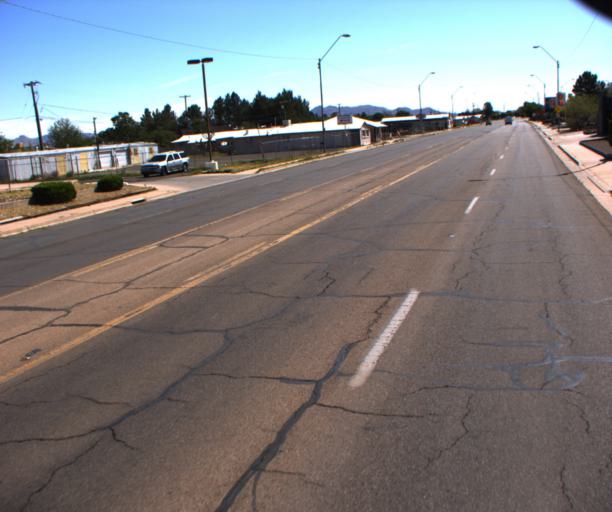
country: US
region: Arizona
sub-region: Cochise County
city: Pirtleville
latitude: 31.3506
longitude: -109.5618
